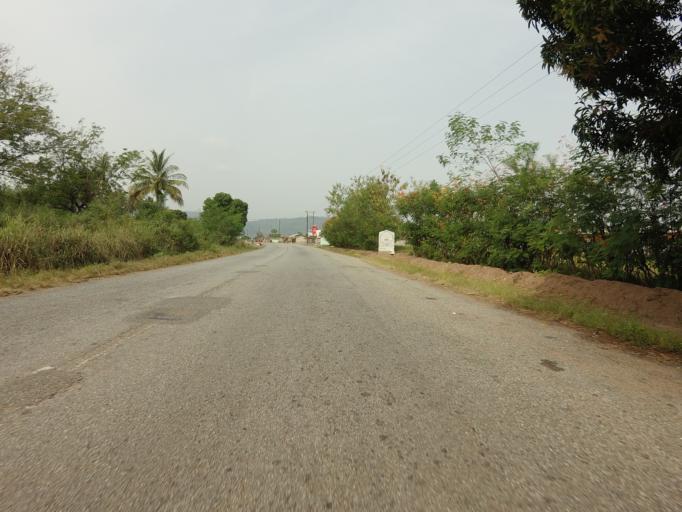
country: GH
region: Volta
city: Ho
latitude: 6.5758
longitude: 0.3348
